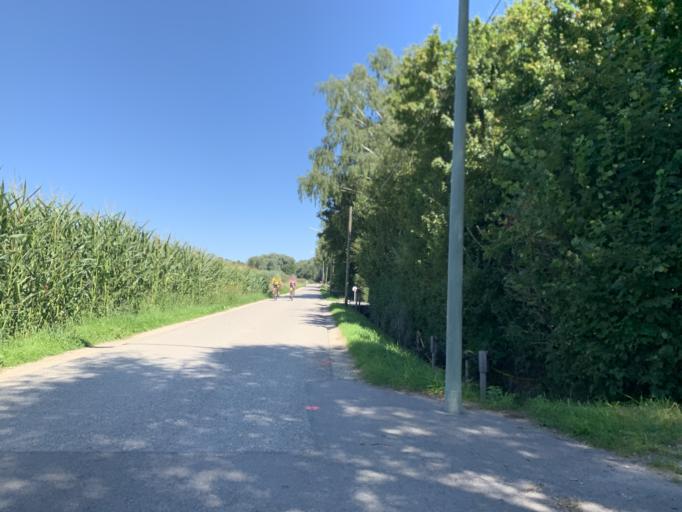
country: DE
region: Bavaria
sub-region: Upper Bavaria
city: Freising
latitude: 48.3901
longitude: 11.7180
